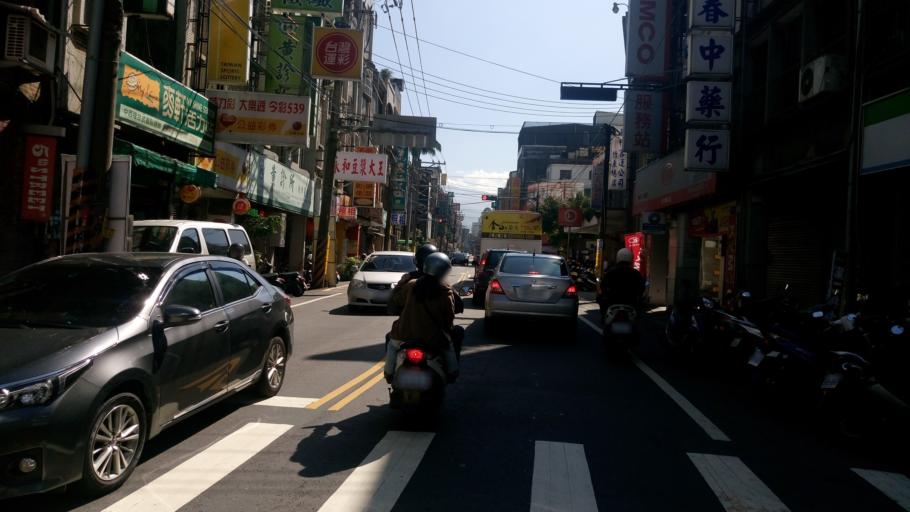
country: TW
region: Taiwan
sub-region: Hsinchu
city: Zhubei
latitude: 24.7401
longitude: 121.0856
